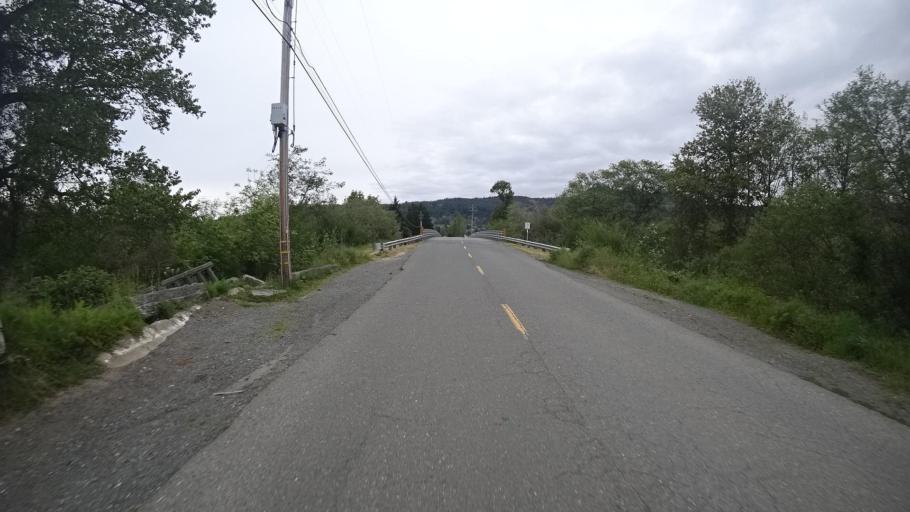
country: US
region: California
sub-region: Humboldt County
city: Blue Lake
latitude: 40.8752
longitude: -123.9929
